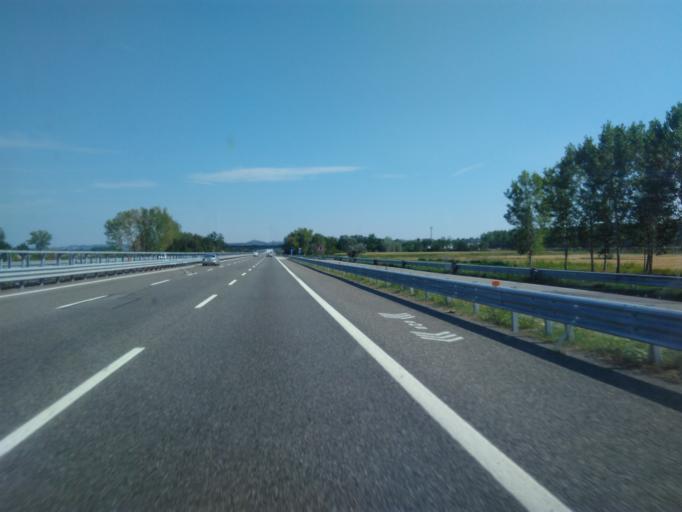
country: IT
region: Piedmont
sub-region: Provincia di Alessandria
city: Mirabello Monferrato
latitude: 45.0490
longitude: 8.5217
